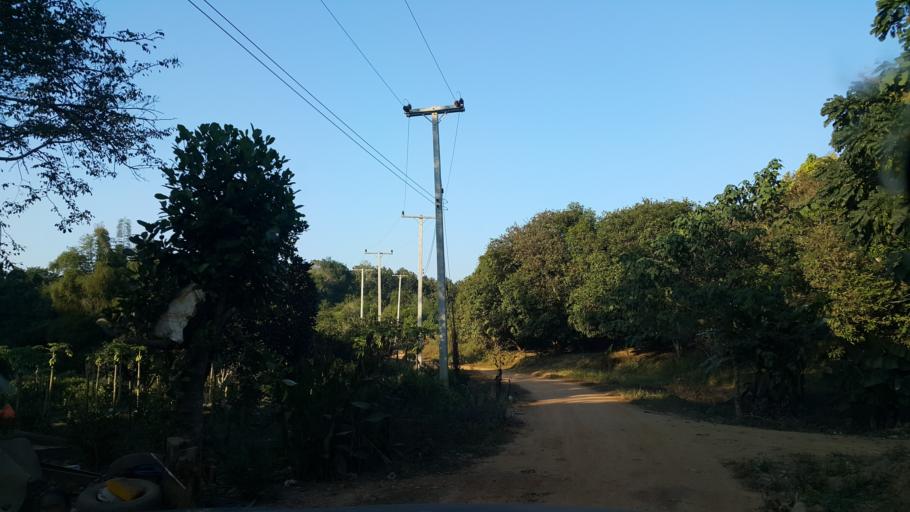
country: TH
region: Sukhothai
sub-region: Amphoe Si Satchanalai
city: Si Satchanalai
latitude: 17.5915
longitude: 99.6158
